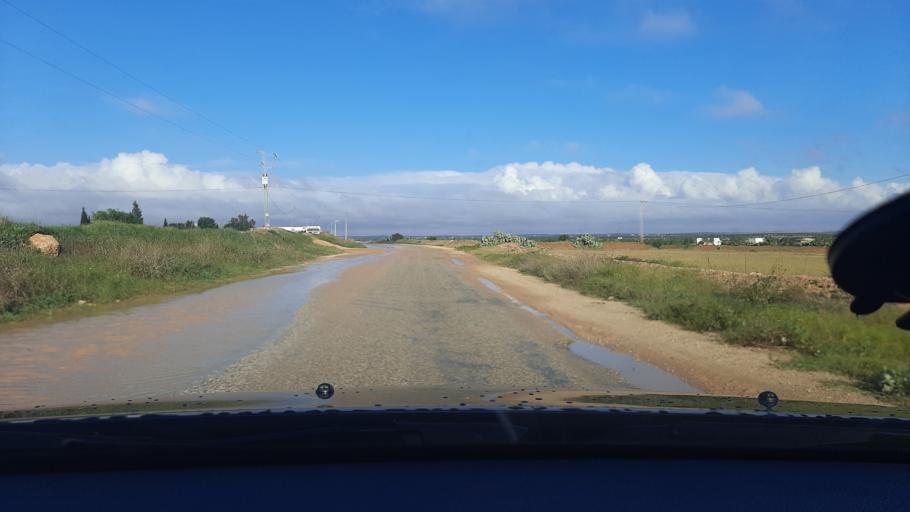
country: TN
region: Safaqis
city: Sfax
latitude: 34.8804
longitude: 10.6328
